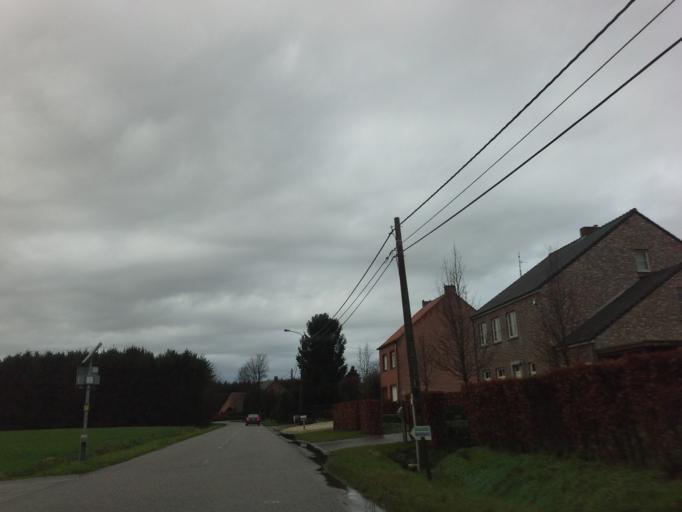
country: BE
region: Flanders
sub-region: Provincie Antwerpen
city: Meerhout
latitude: 51.1211
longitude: 5.0714
